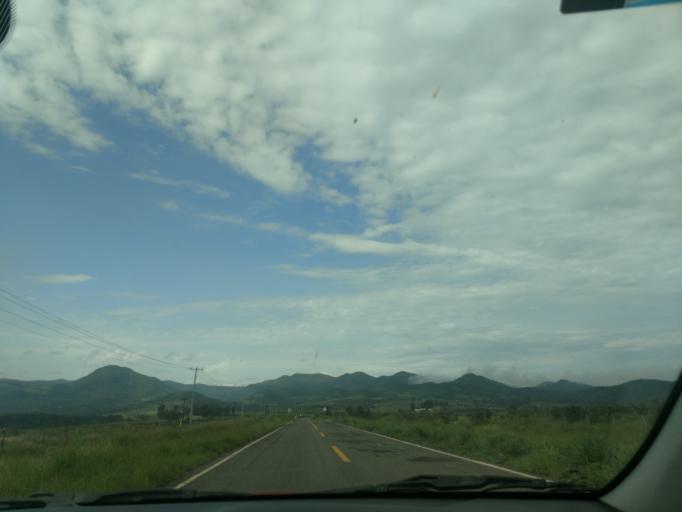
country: MX
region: Jalisco
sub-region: Atengo
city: Soyatlan del Oro
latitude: 20.5313
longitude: -104.3190
